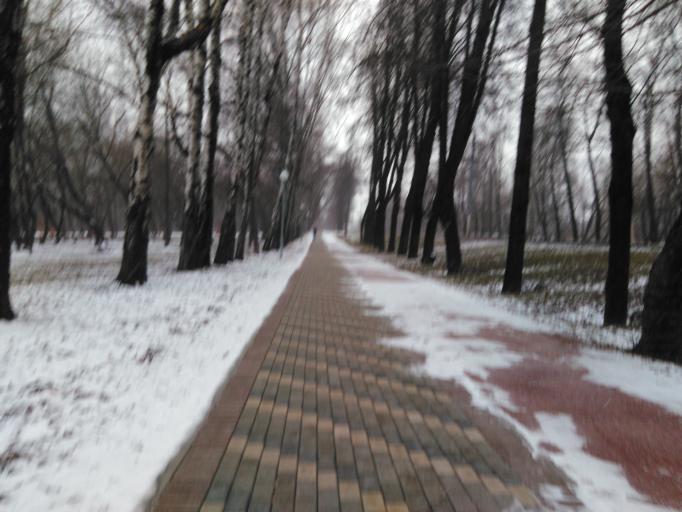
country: RU
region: Moskovskaya
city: Kur'yanovo
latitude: 55.6335
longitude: 37.6954
